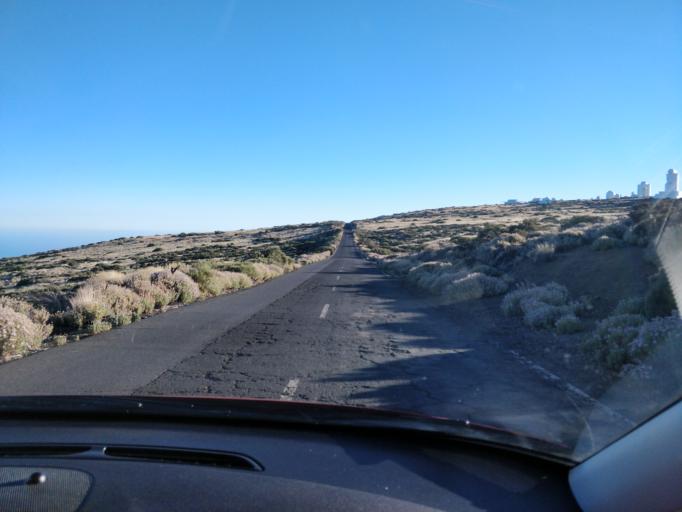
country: ES
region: Canary Islands
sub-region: Provincia de Santa Cruz de Tenerife
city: Guimar
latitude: 28.3050
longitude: -16.5021
